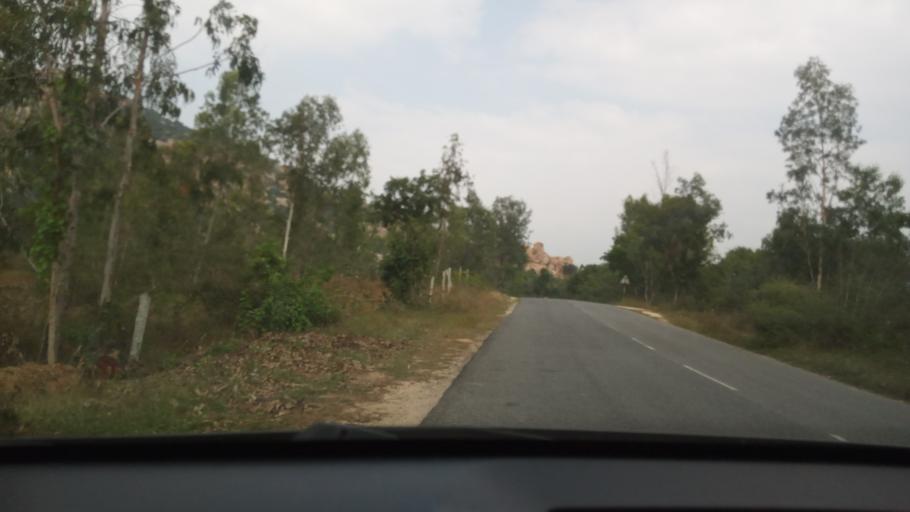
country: IN
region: Andhra Pradesh
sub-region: Chittoor
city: Pakala
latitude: 13.6573
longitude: 78.8599
